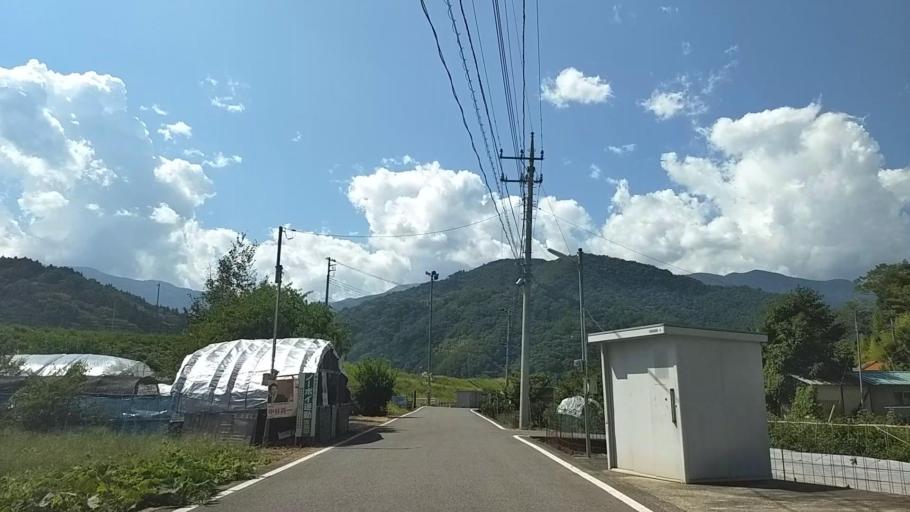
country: JP
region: Yamanashi
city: Ryuo
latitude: 35.5131
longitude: 138.4611
